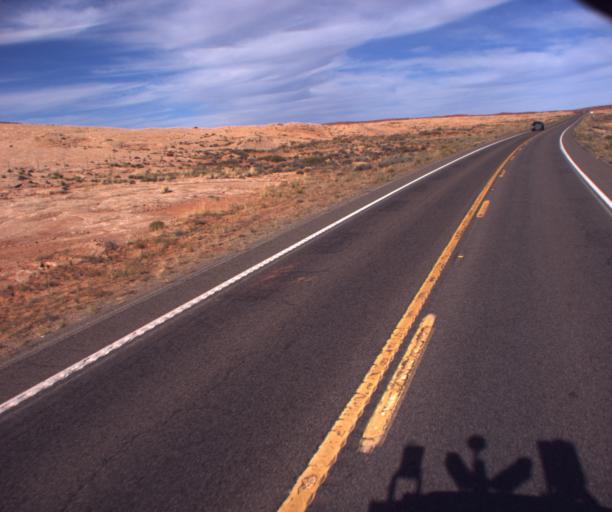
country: US
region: Arizona
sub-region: Navajo County
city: Kayenta
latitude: 36.8859
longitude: -109.8135
